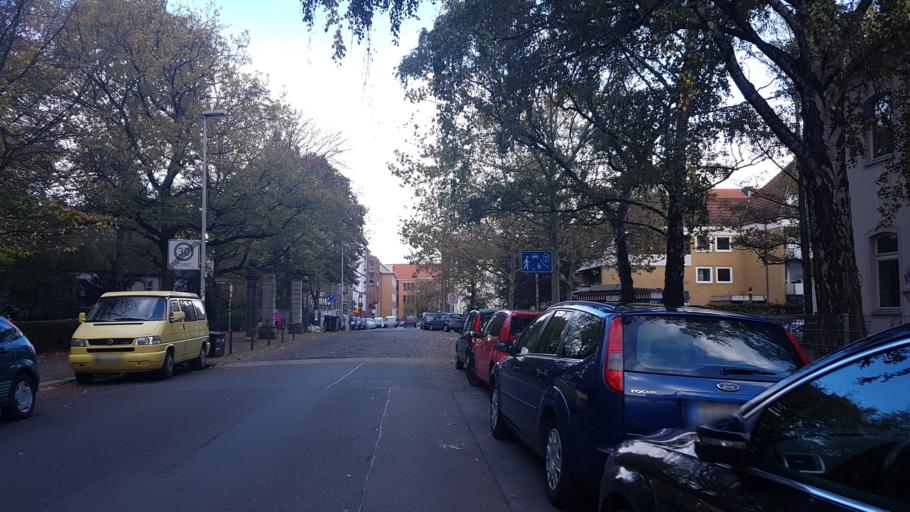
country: DE
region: Lower Saxony
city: Hannover
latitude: 52.3642
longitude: 9.7152
